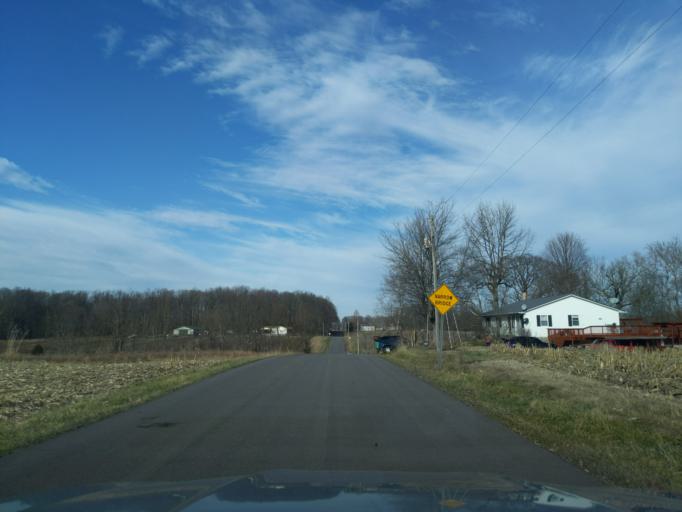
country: US
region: Indiana
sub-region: Decatur County
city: Greensburg
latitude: 39.2254
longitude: -85.4295
